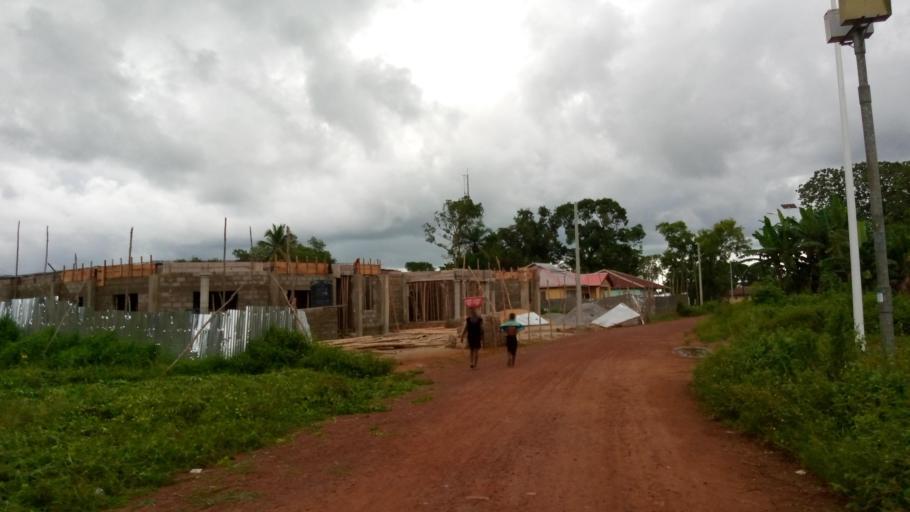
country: SL
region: Southern Province
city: Moyamba
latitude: 8.1626
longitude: -12.4379
